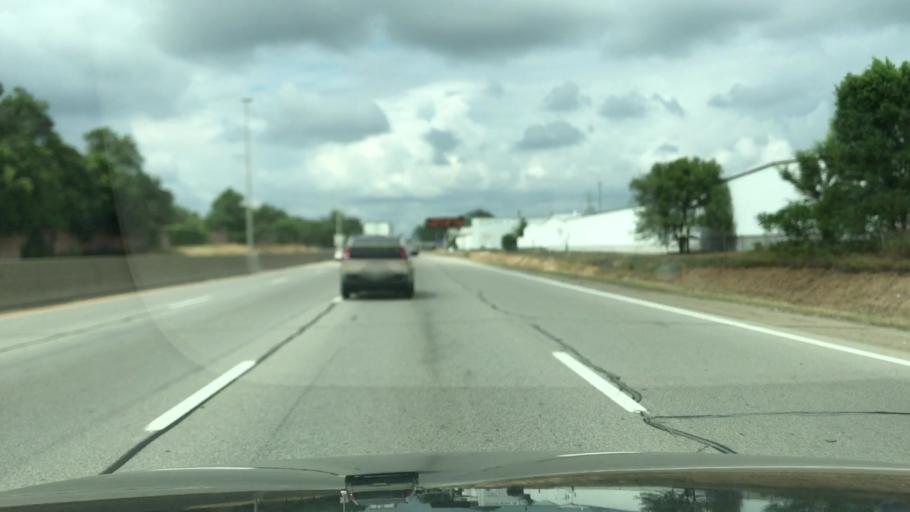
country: US
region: Michigan
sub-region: Kent County
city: Wyoming
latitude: 42.9012
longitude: -85.6775
